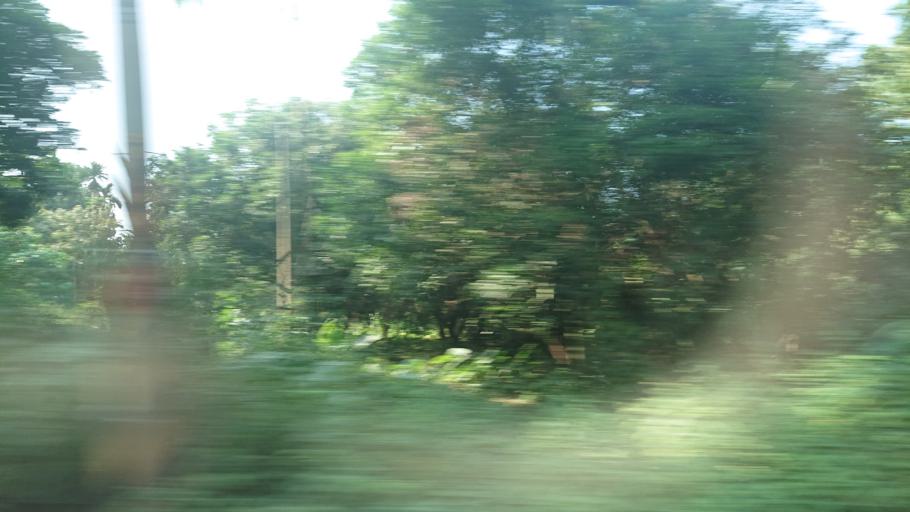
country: TW
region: Taiwan
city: Lugu
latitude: 23.7223
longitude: 120.6690
